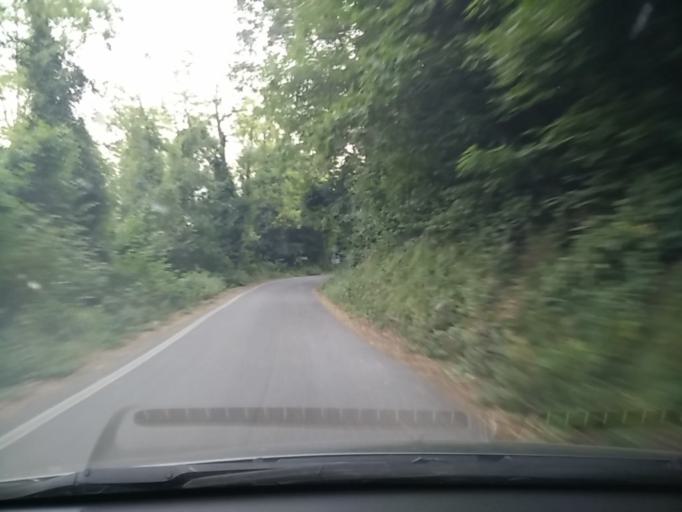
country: IT
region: Lombardy
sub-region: Provincia di Pavia
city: Susella
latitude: 44.9160
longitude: 9.0987
